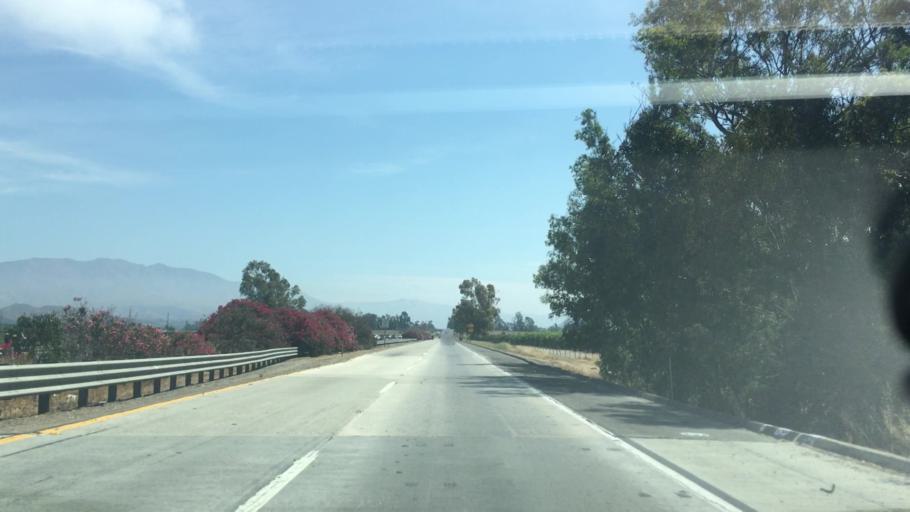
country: US
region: California
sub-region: Ventura County
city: Saticoy
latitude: 34.3016
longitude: -119.1361
